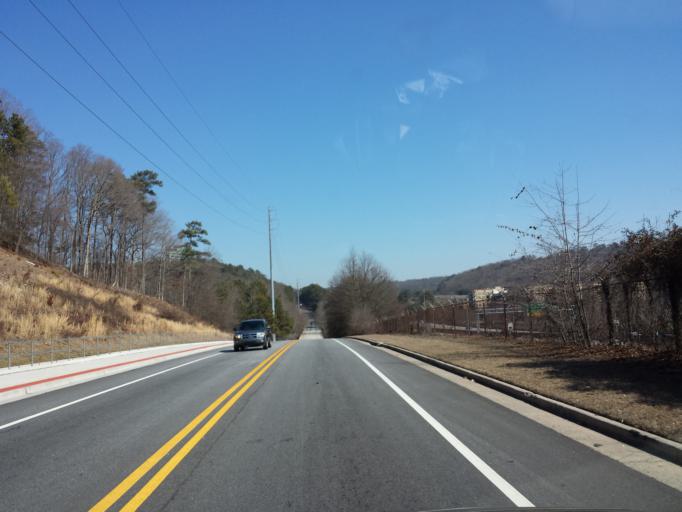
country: US
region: Georgia
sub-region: Cobb County
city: Vinings
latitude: 33.9009
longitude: -84.4461
